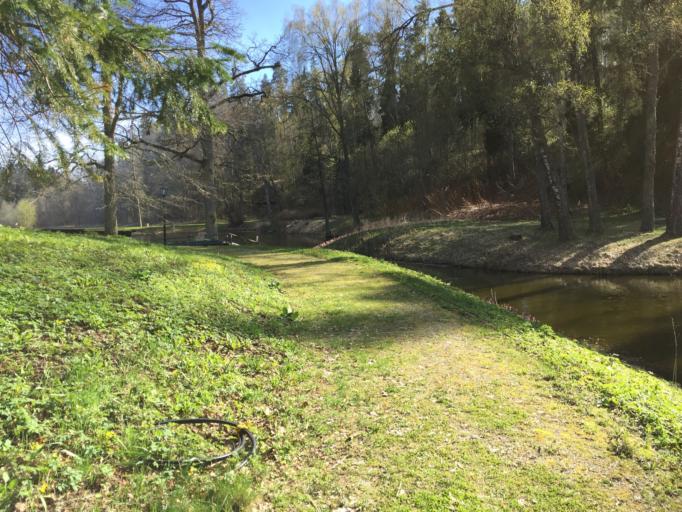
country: EE
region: Vorumaa
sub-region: Antsla vald
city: Vana-Antsla
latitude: 57.9022
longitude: 26.2788
